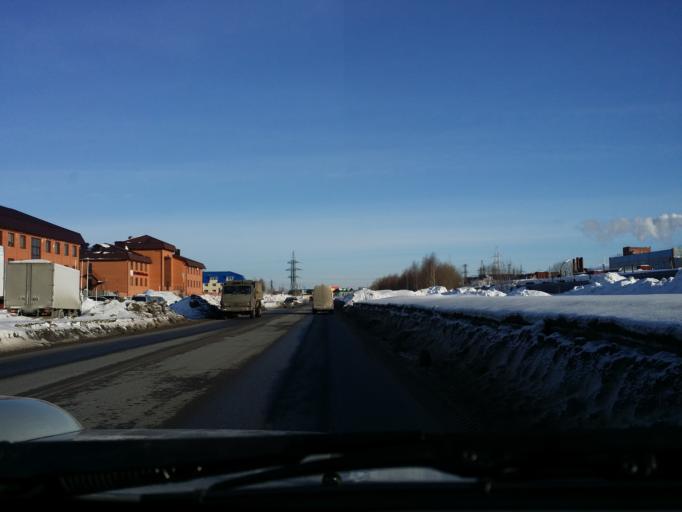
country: RU
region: Khanty-Mansiyskiy Avtonomnyy Okrug
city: Nizhnevartovsk
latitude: 60.9486
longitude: 76.6180
